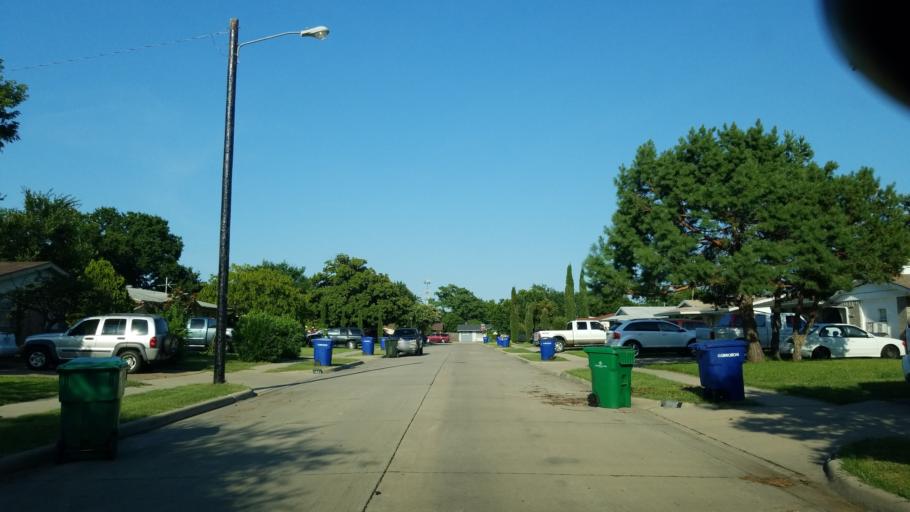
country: US
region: Texas
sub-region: Dallas County
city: Carrollton
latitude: 32.9432
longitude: -96.8939
